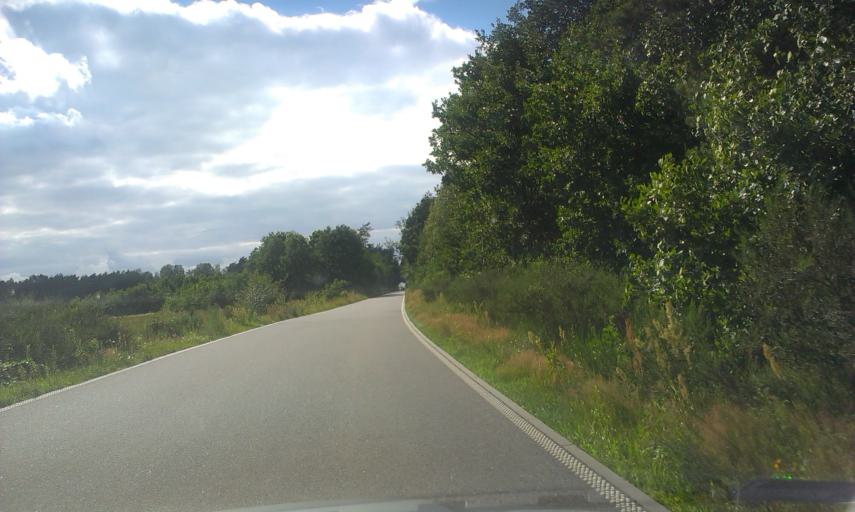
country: PL
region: Masovian Voivodeship
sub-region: Powiat zyrardowski
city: Radziejowice
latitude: 51.9677
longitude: 20.5909
